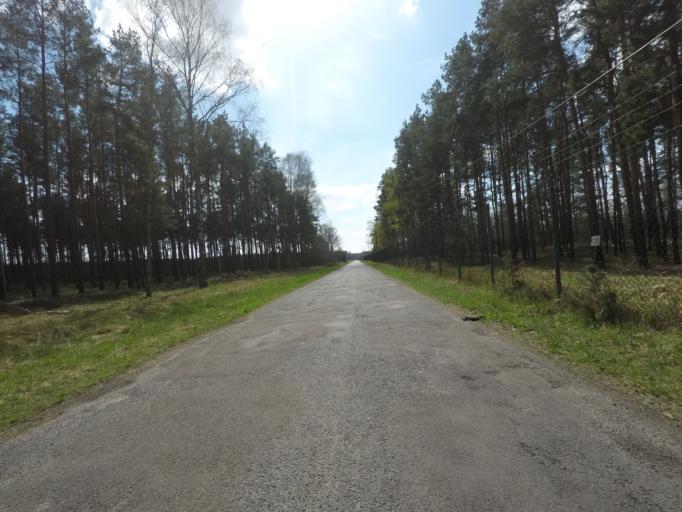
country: DE
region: Brandenburg
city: Melchow
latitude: 52.8281
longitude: 13.7198
